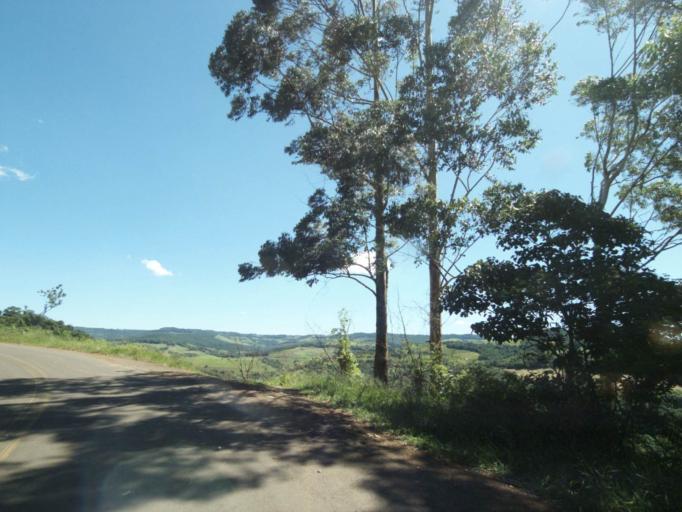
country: AR
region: Misiones
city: Bernardo de Irigoyen
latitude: -26.1880
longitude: -53.3647
